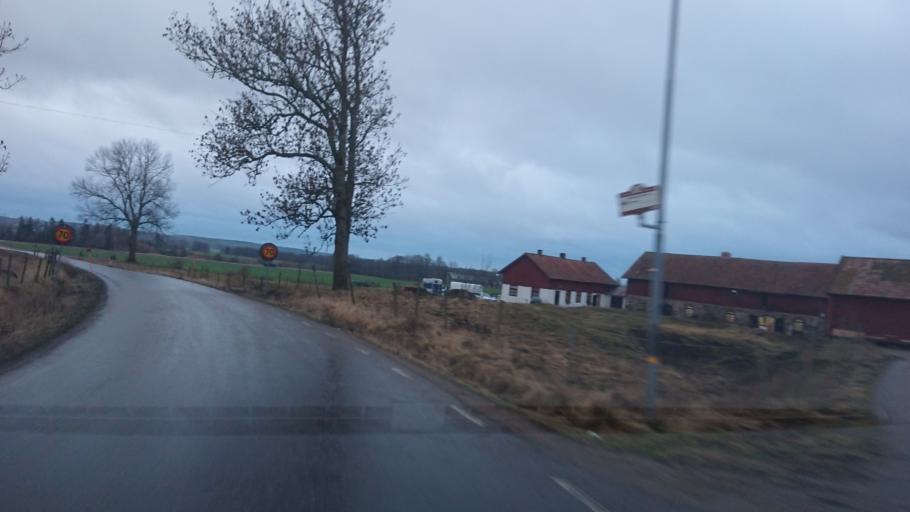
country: SE
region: Uppsala
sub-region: Uppsala Kommun
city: Gamla Uppsala
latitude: 59.9546
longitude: 17.6055
